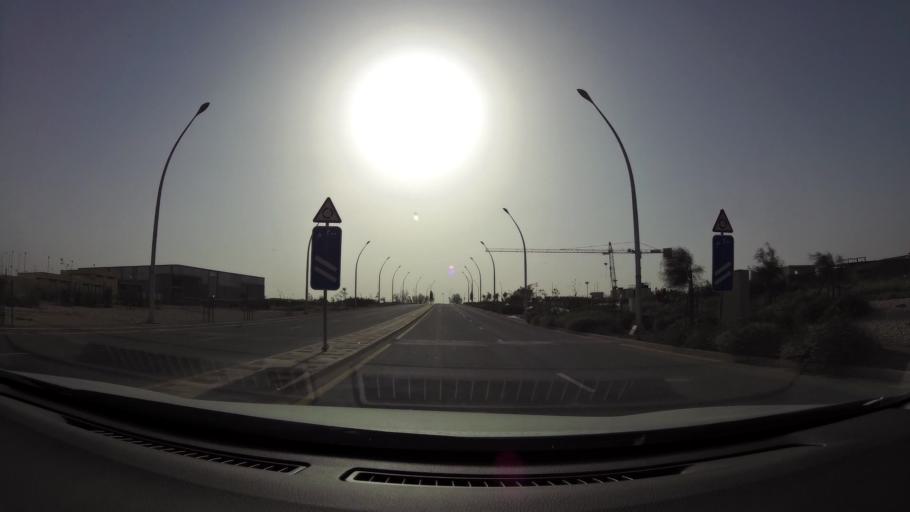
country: QA
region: Baladiyat ar Rayyan
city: Ar Rayyan
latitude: 25.3270
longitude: 51.4325
